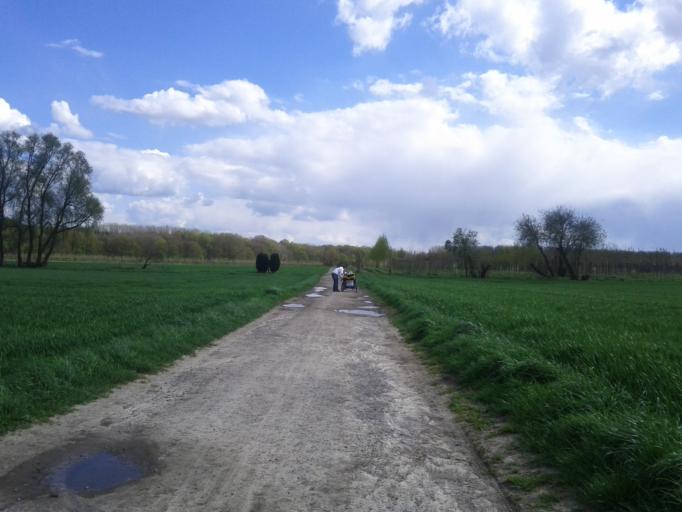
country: DE
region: North Rhine-Westphalia
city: Lanstrop
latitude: 51.5727
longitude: 7.5759
